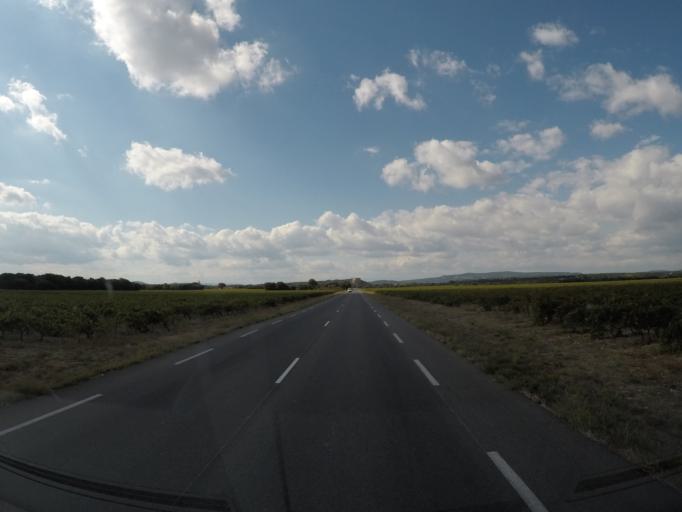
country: FR
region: Rhone-Alpes
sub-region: Departement de la Drome
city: Suze-la-Rousse
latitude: 44.2869
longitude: 4.8617
